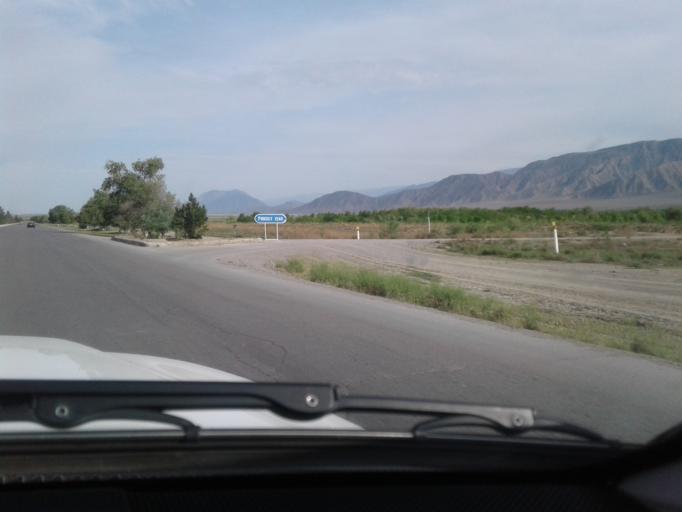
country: TM
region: Ahal
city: Arcabil
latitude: 38.1889
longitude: 57.8475
